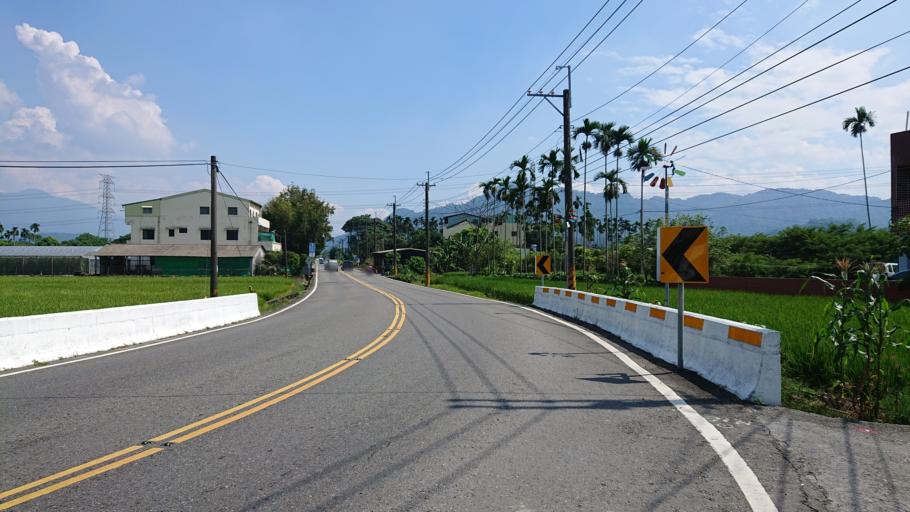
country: TW
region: Taiwan
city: Lugu
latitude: 23.8148
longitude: 120.7247
